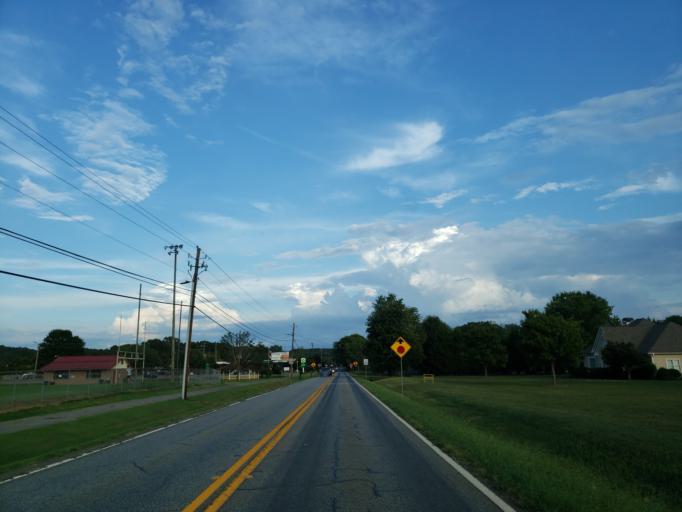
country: US
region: Georgia
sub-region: Bartow County
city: Cartersville
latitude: 34.2340
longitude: -84.8671
